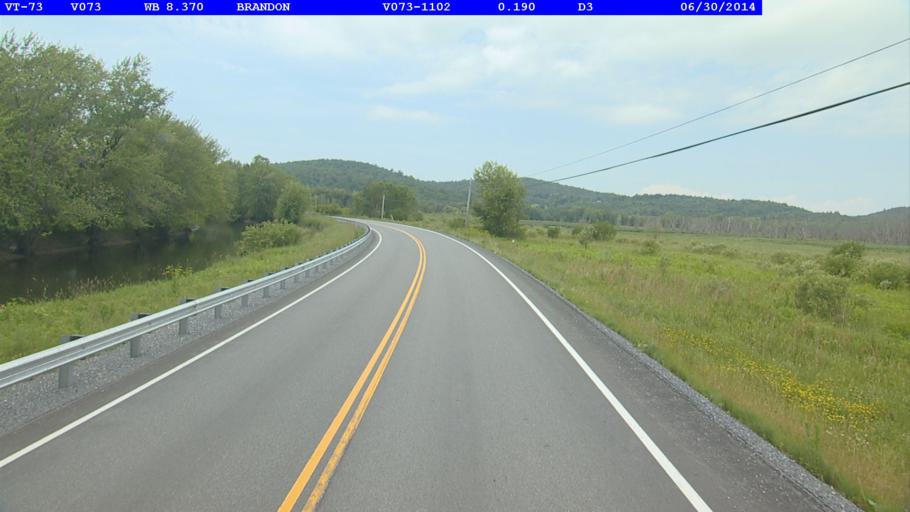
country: US
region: Vermont
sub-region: Rutland County
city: Brandon
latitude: 43.8072
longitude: -73.1430
